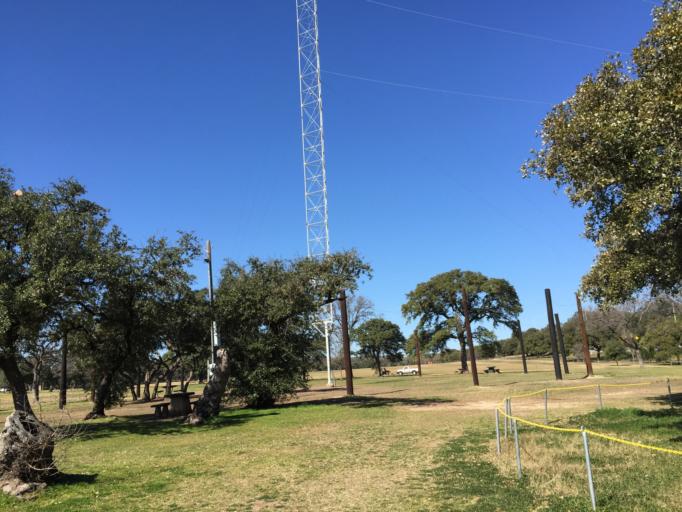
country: US
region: Texas
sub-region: Travis County
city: Rollingwood
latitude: 30.2662
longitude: -97.7708
